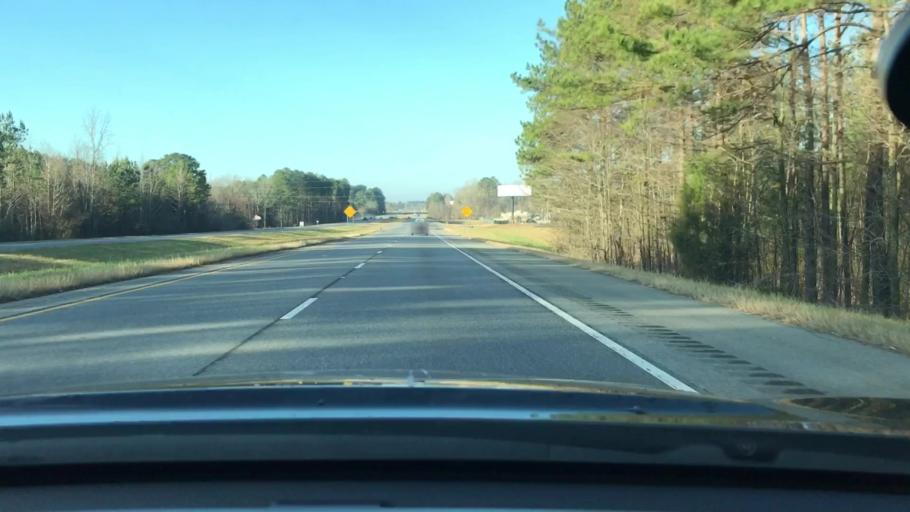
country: US
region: Alabama
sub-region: Shelby County
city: Westover
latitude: 33.3550
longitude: -86.5198
